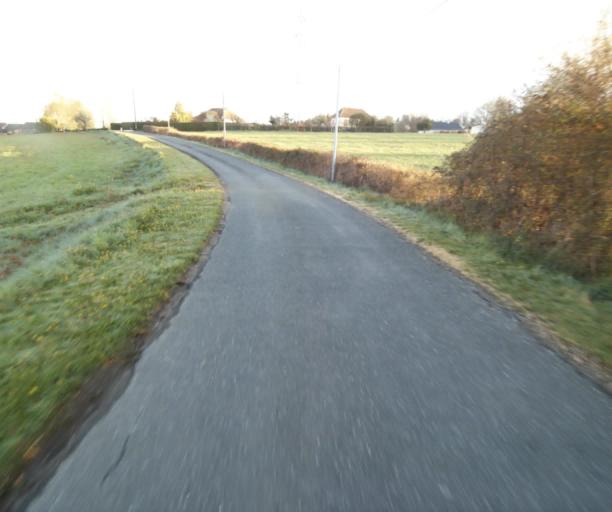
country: FR
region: Limousin
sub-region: Departement de la Correze
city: Correze
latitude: 45.3195
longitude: 1.8384
